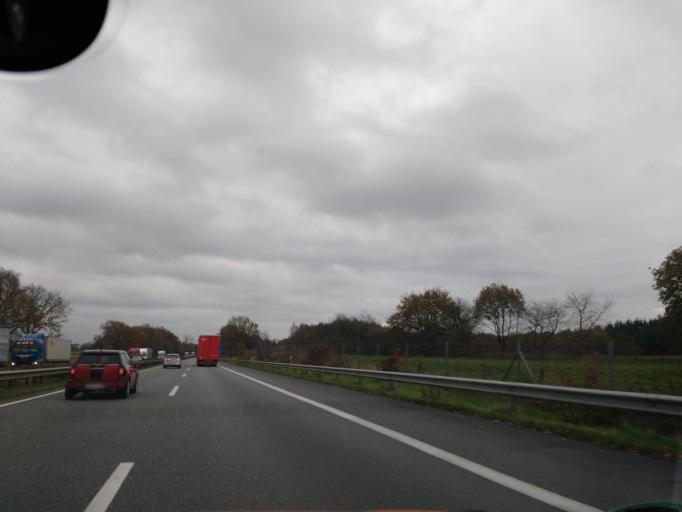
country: DE
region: Lower Saxony
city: Verden
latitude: 52.9685
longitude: 9.2343
